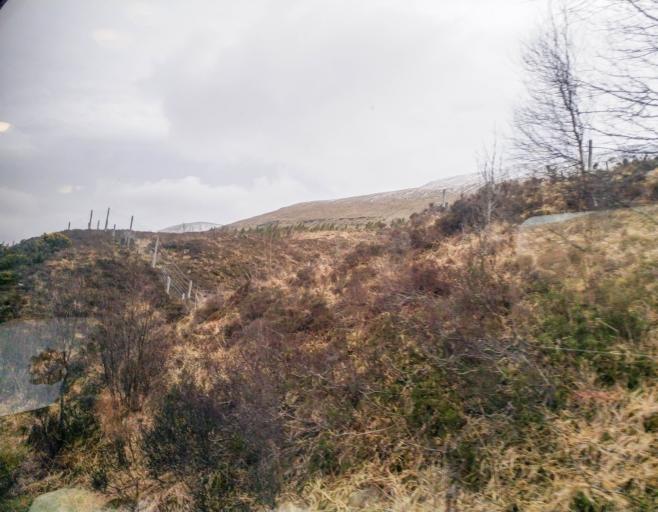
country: GB
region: Scotland
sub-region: Highland
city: Spean Bridge
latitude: 56.5679
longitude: -4.6971
